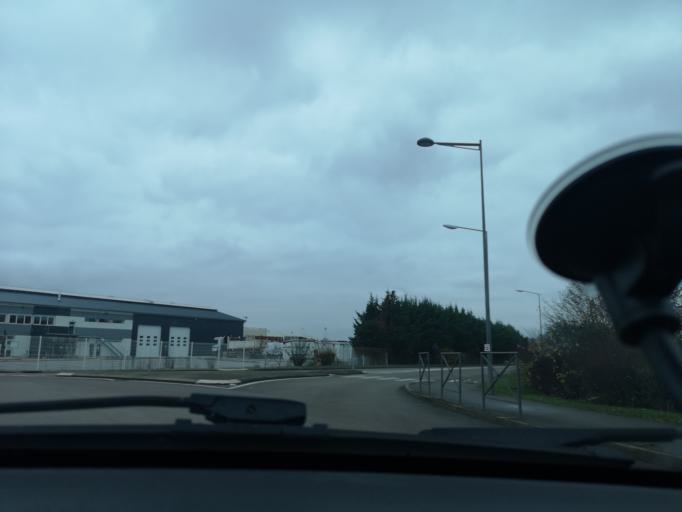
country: FR
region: Bourgogne
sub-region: Departement de Saone-et-Loire
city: Virey-le-Grand
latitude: 46.8242
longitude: 4.8641
